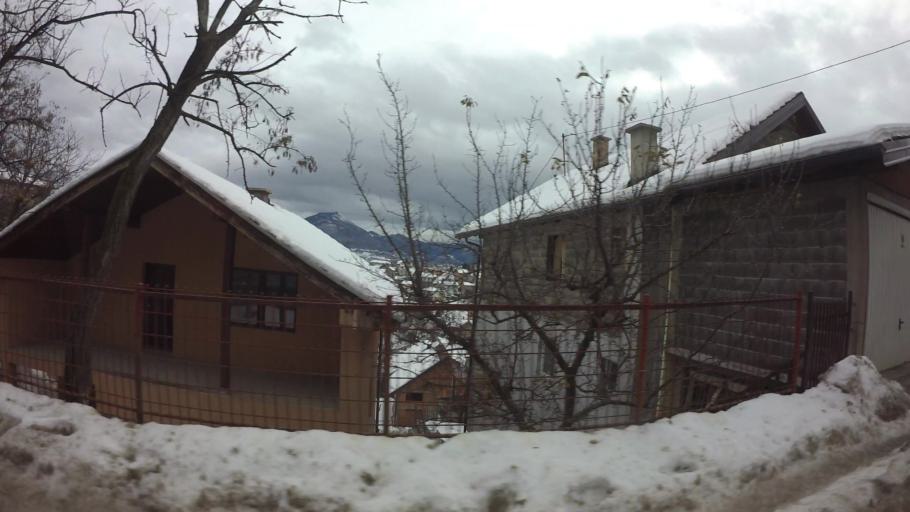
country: BA
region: Federation of Bosnia and Herzegovina
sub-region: Kanton Sarajevo
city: Sarajevo
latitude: 43.8586
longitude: 18.3555
